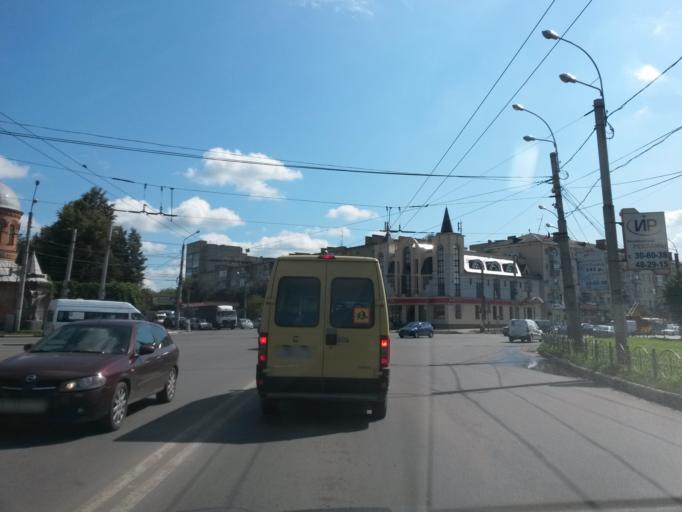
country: RU
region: Ivanovo
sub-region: Gorod Ivanovo
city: Ivanovo
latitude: 57.0103
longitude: 40.9878
